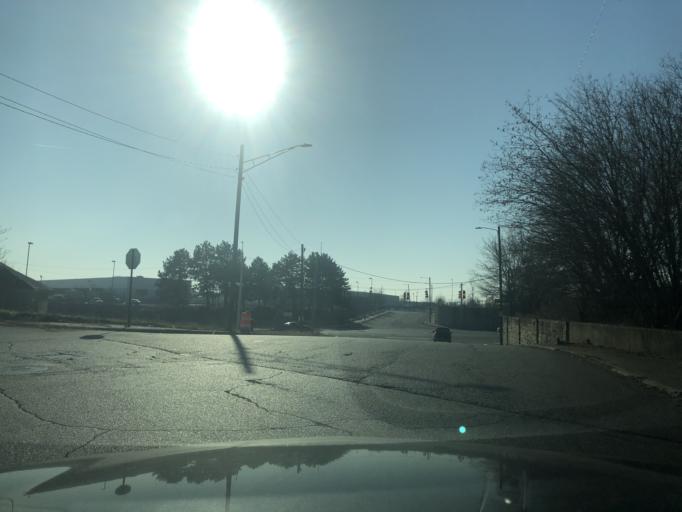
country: US
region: Michigan
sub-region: Wayne County
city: Detroit
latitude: 42.3320
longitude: -83.1019
